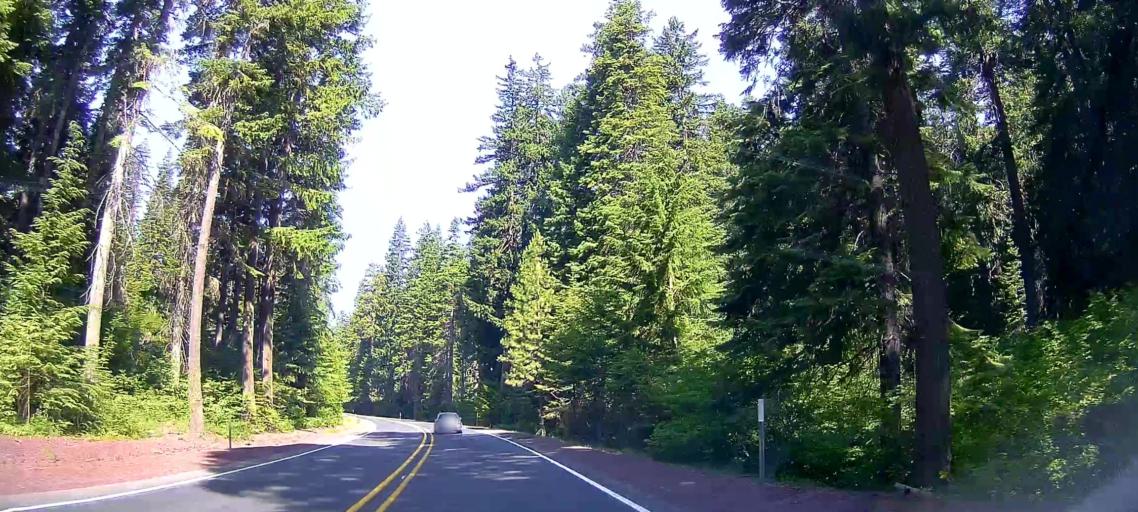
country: US
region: Oregon
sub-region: Jefferson County
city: Warm Springs
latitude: 45.1133
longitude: -121.5679
